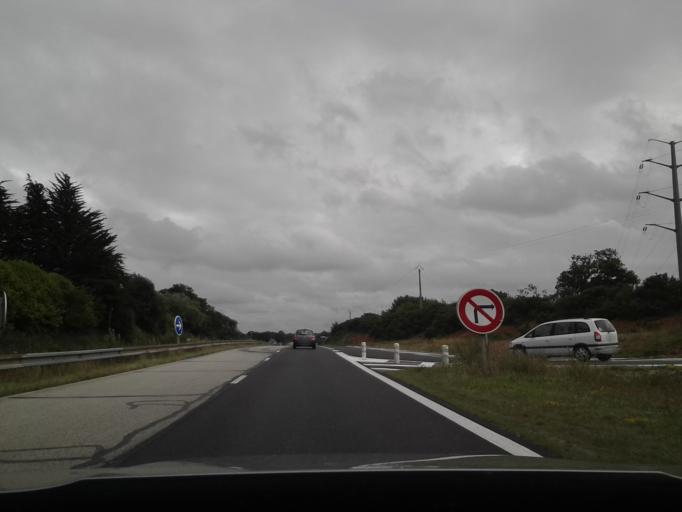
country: FR
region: Lower Normandy
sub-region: Departement de la Manche
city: La Glacerie
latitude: 49.5834
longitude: -1.5915
